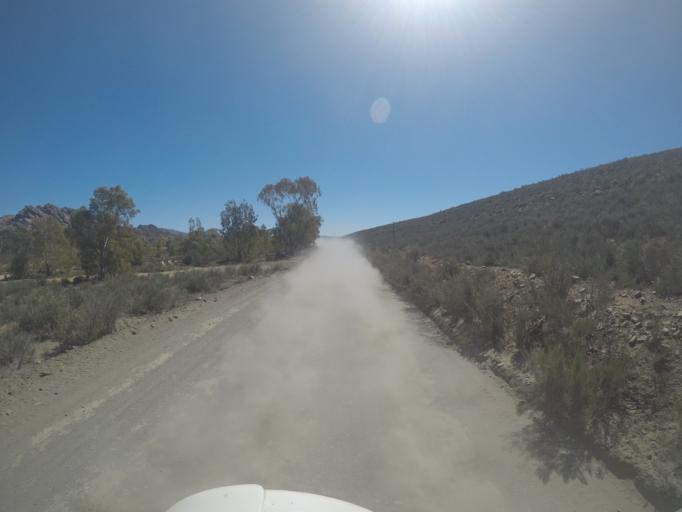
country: ZA
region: Western Cape
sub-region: Cape Winelands District Municipality
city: Ceres
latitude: -32.8146
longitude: 19.4519
